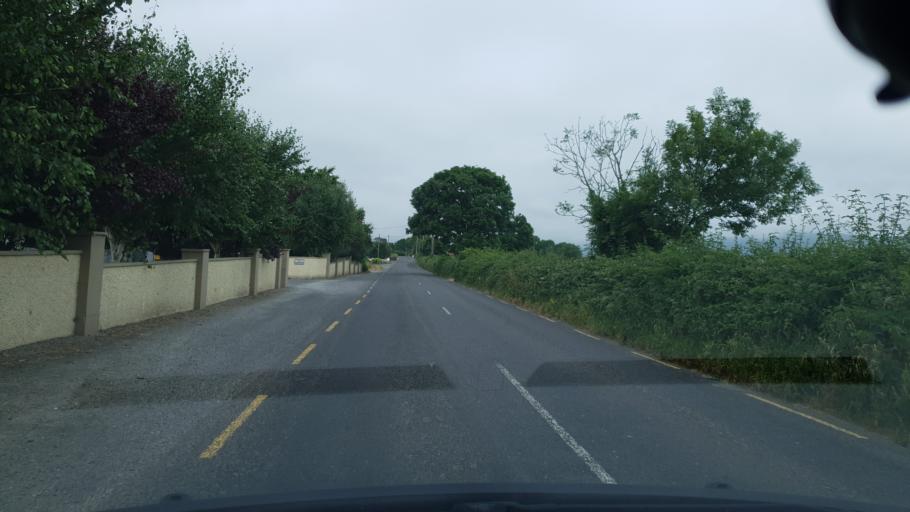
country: IE
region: Munster
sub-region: Ciarrai
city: Tralee
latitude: 52.1636
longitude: -9.6299
